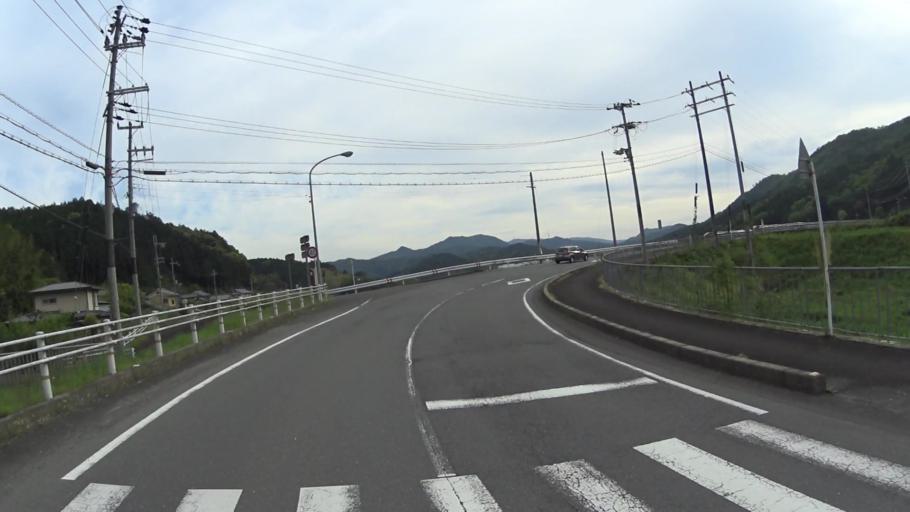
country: JP
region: Kyoto
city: Kameoka
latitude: 35.1034
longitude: 135.5169
